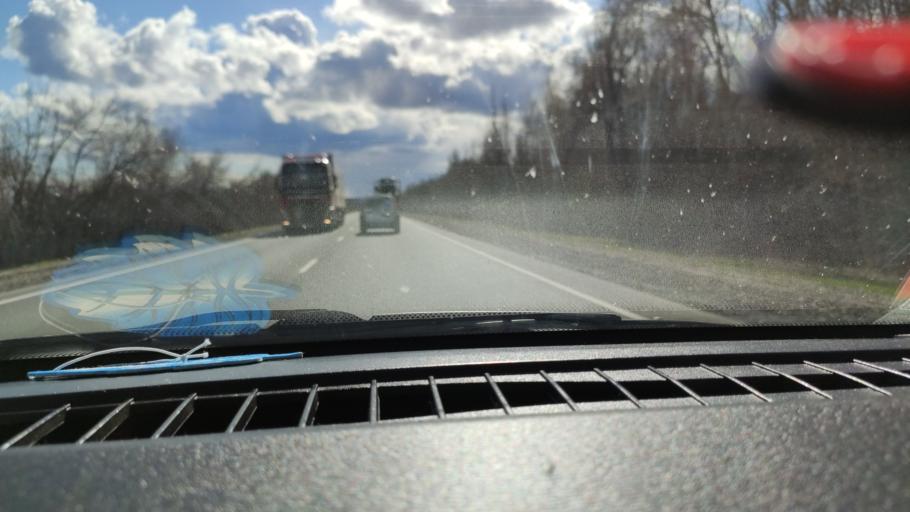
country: RU
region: Saratov
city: Khvalynsk
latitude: 52.5963
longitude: 48.1382
